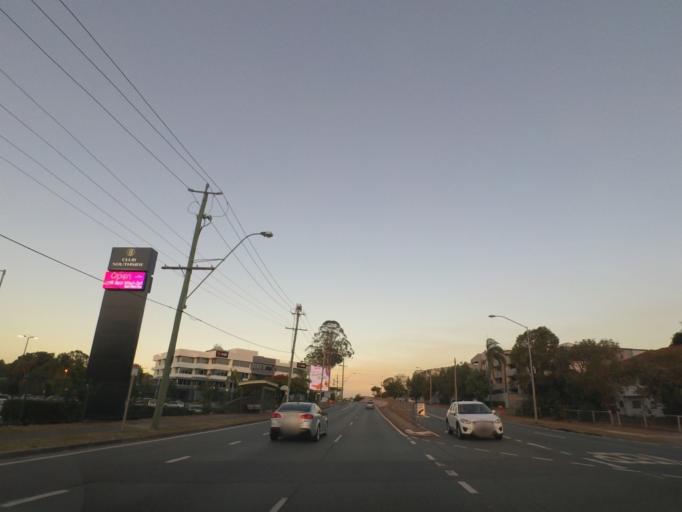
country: AU
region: Queensland
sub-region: Brisbane
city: Upper Mount Gravatt
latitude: -27.5588
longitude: 153.0840
